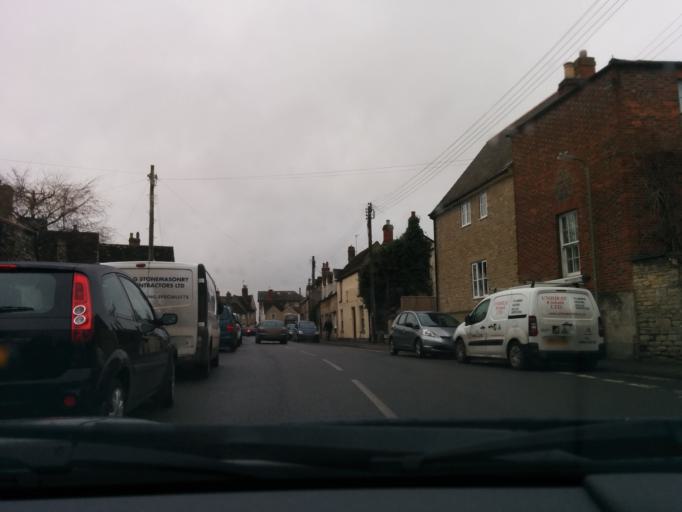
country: GB
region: England
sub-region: Oxfordshire
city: Eynsham
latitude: 51.7803
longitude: -1.3715
